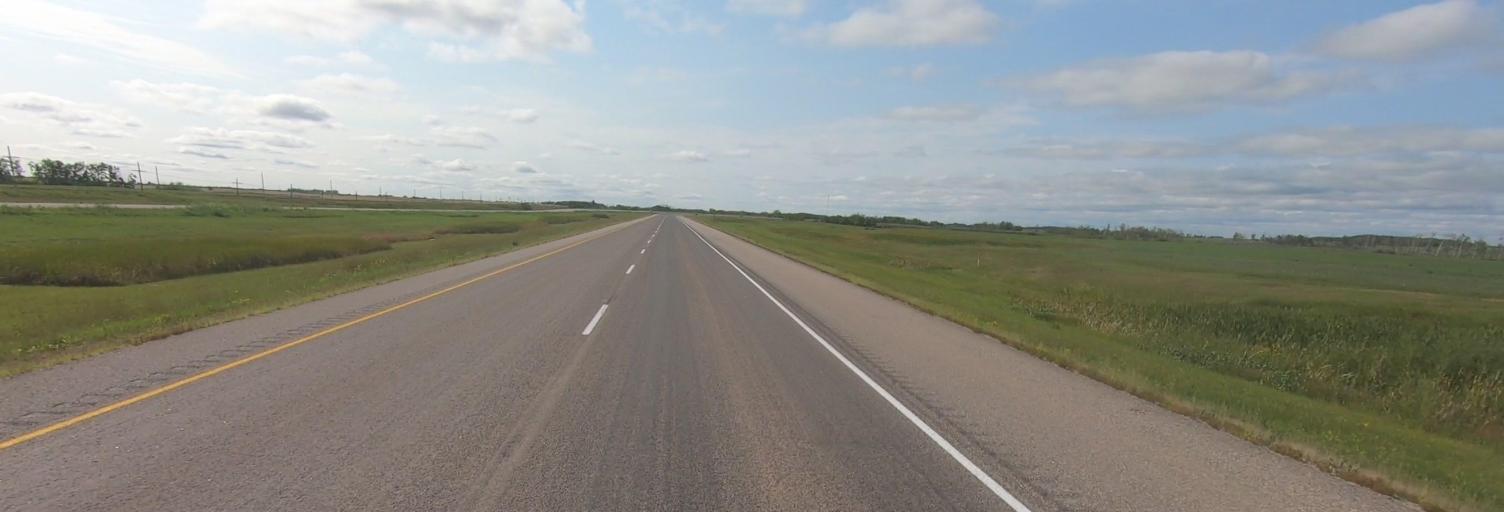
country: CA
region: Saskatchewan
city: Moosomin
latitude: 50.0166
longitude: -101.3375
